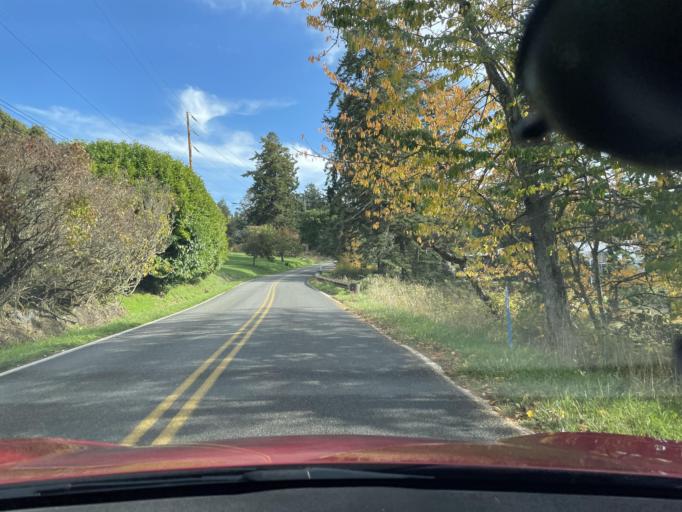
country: US
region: Washington
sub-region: San Juan County
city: Friday Harbor
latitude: 48.5200
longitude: -123.0002
